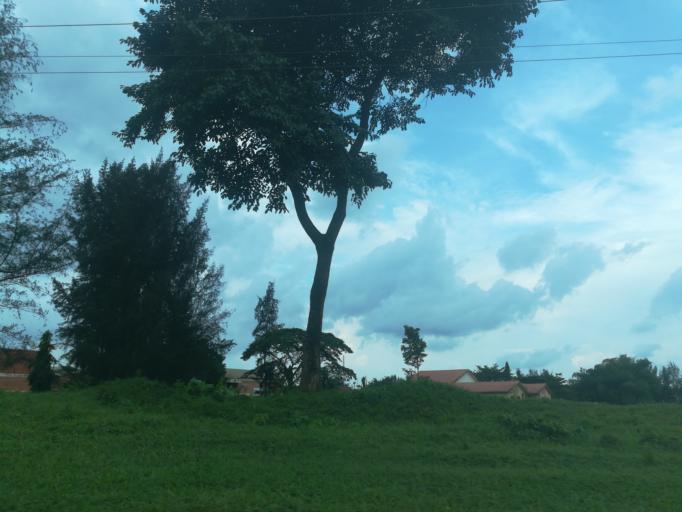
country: NG
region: Lagos
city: Ikorodu
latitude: 6.6373
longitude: 3.5215
